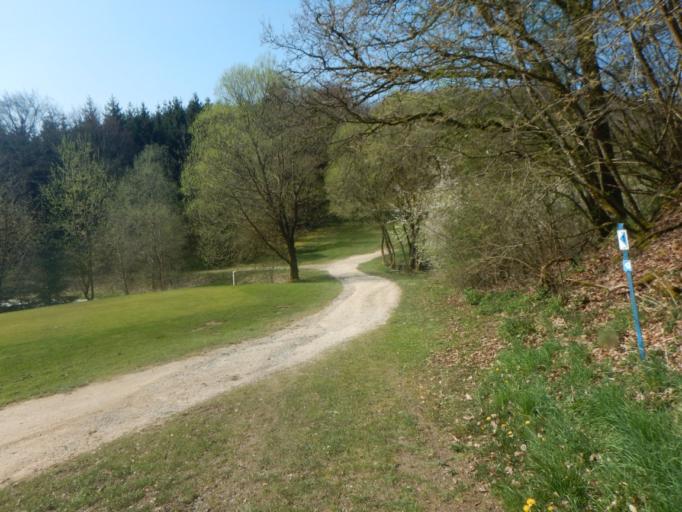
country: LU
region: Diekirch
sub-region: Canton de Clervaux
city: Clervaux
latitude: 50.0571
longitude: 5.9972
